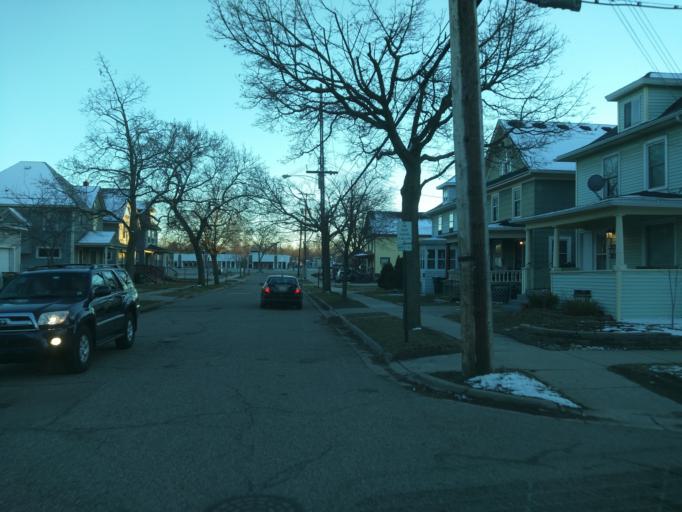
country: US
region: Michigan
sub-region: Ingham County
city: Lansing
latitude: 42.7347
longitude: -84.5313
